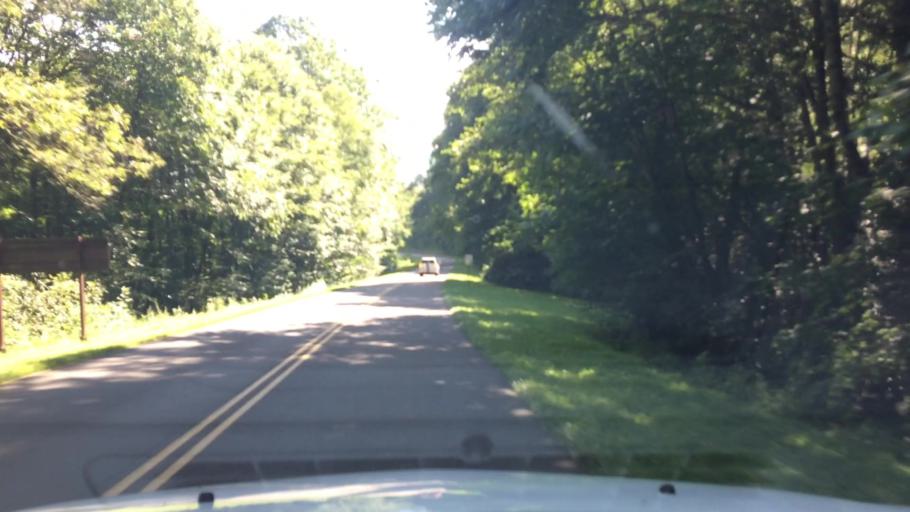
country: US
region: North Carolina
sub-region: Watauga County
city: Blowing Rock
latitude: 36.1440
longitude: -81.7166
